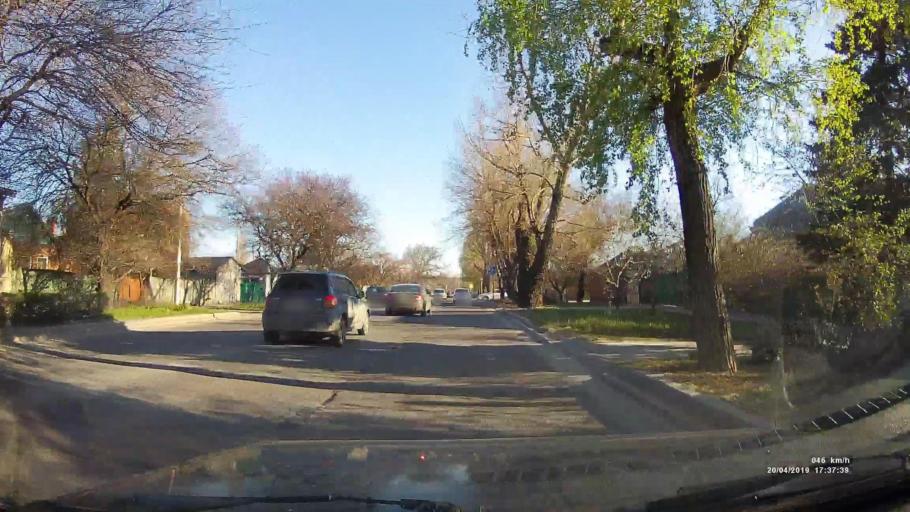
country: RU
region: Rostov
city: Imeni Chkalova
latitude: 47.2509
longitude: 39.7952
